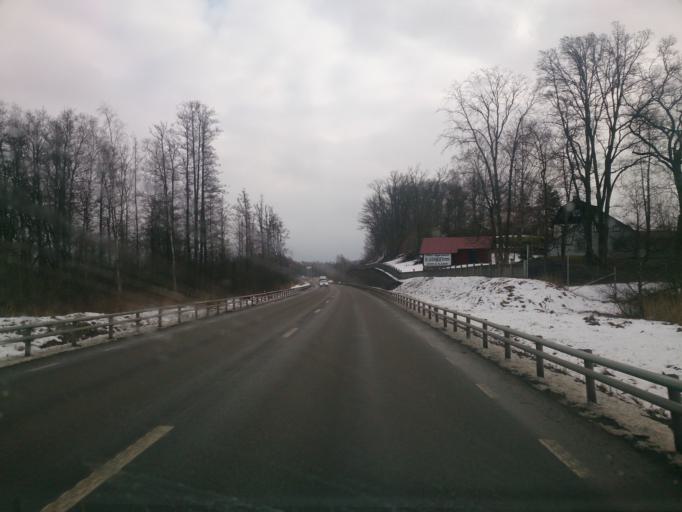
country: SE
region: OEstergoetland
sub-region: Atvidabergs Kommun
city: Atvidaberg
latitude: 58.1988
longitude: 16.0103
